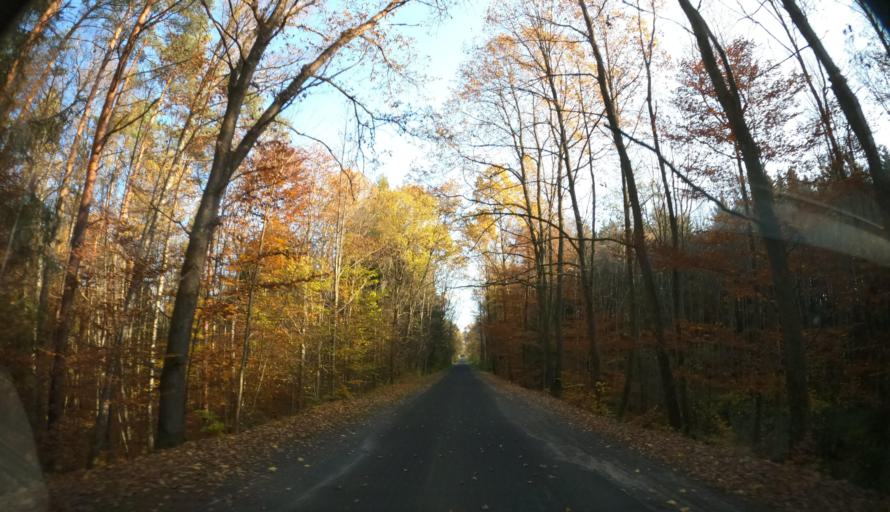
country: PL
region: West Pomeranian Voivodeship
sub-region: Powiat koszalinski
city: Polanow
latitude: 54.2407
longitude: 16.7190
